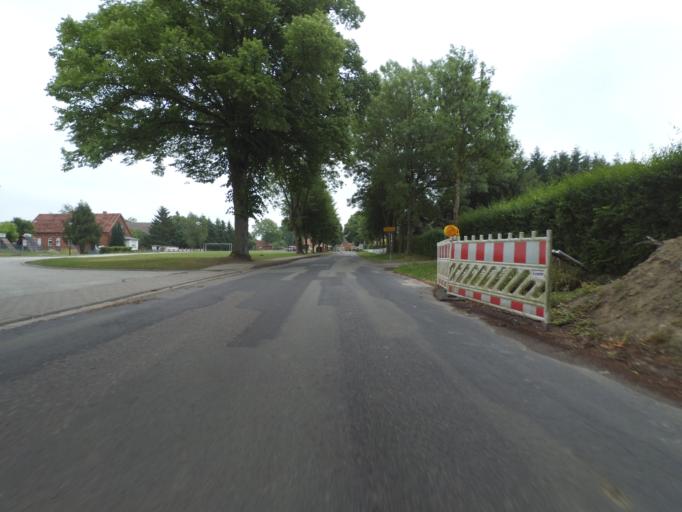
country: DE
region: Mecklenburg-Vorpommern
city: Lubz
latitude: 53.5015
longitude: 12.0057
